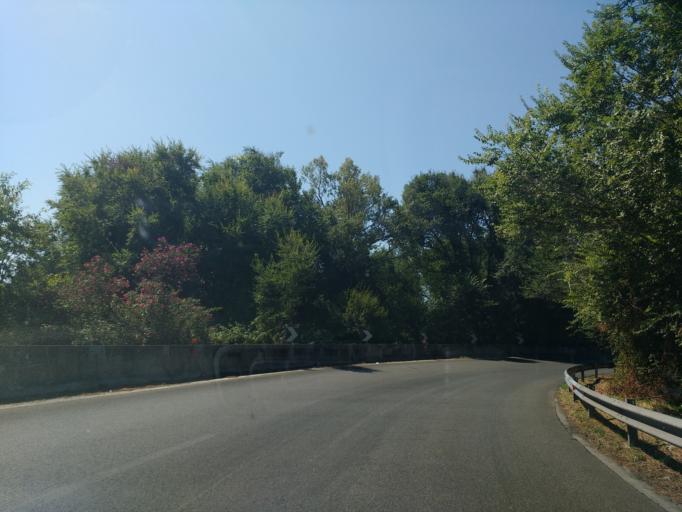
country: IT
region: Latium
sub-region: Citta metropolitana di Roma Capitale
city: Lido di Ostia
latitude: 41.7492
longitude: 12.2894
